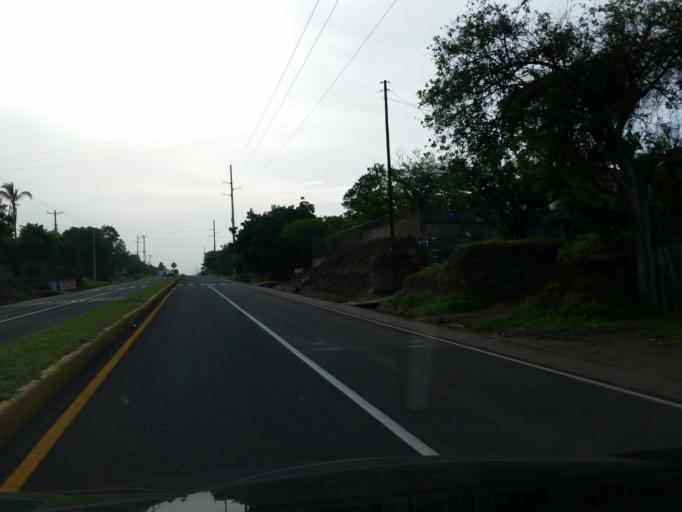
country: NI
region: Granada
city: Granada
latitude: 11.9699
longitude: -86.0184
